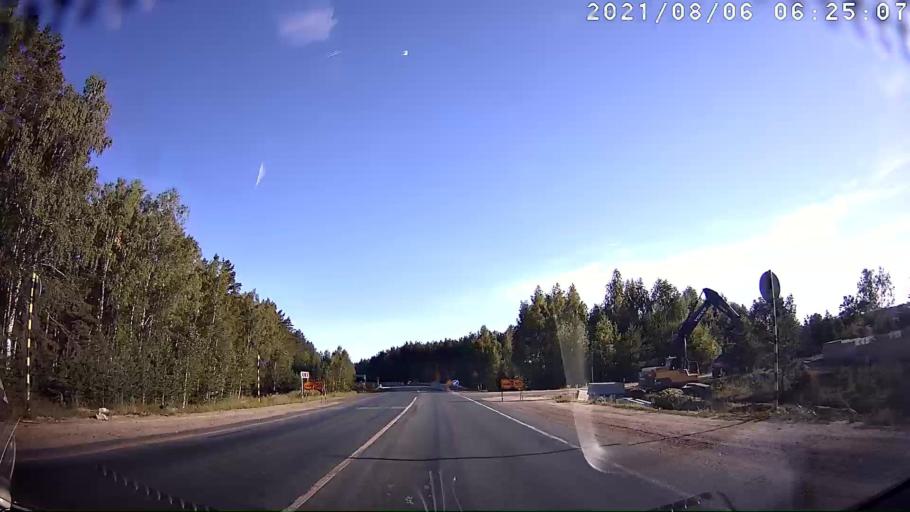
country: RU
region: Mariy-El
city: Krasnogorskiy
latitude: 56.1149
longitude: 48.3457
